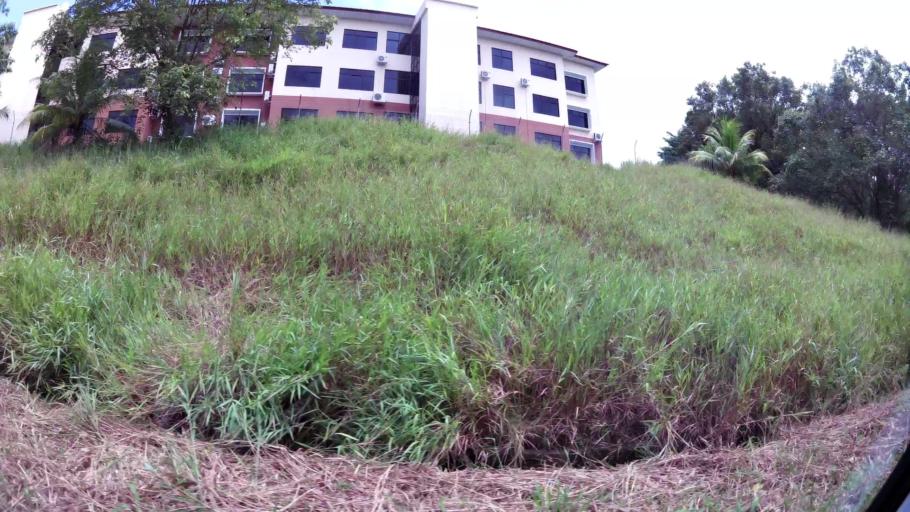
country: BN
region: Brunei and Muara
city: Bandar Seri Begawan
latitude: 4.9040
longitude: 114.9117
